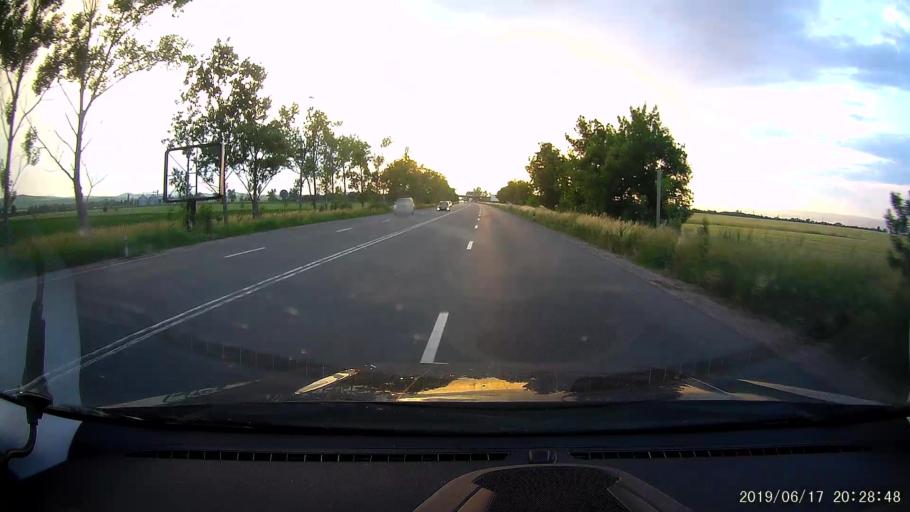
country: BG
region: Sofiya
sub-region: Obshtina Bozhurishte
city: Bozhurishte
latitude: 42.7809
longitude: 23.1721
